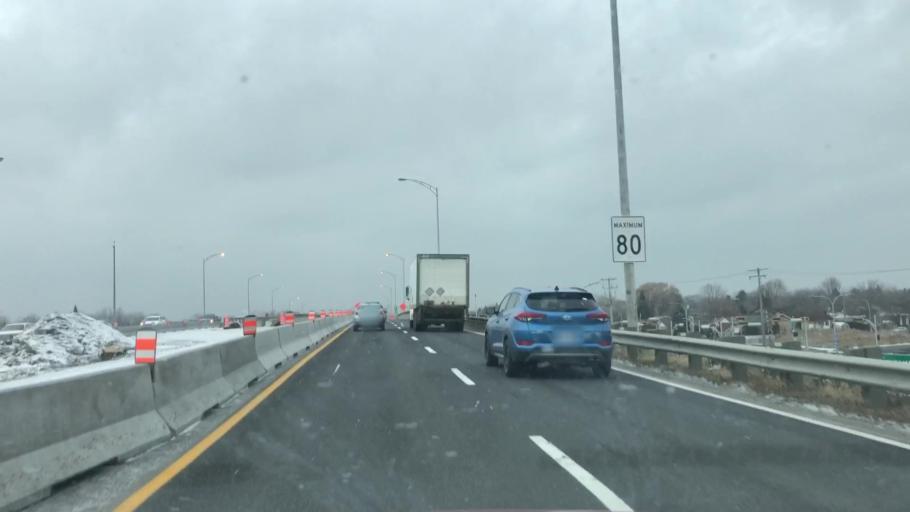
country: CA
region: Quebec
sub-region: Monteregie
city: Brossard
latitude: 45.4554
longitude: -73.4453
